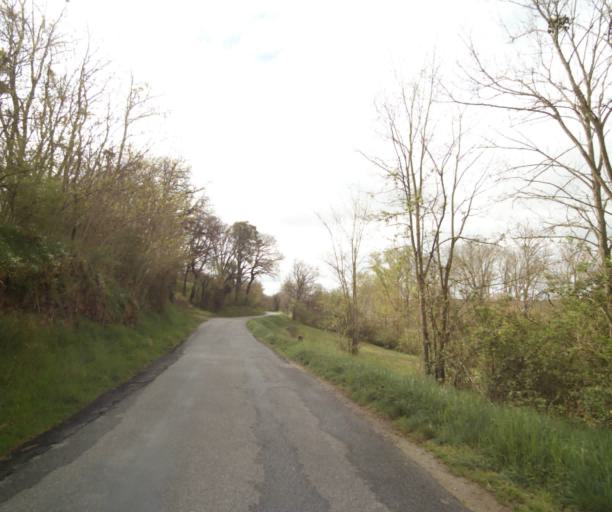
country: FR
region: Midi-Pyrenees
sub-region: Departement de l'Ariege
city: Saverdun
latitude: 43.2394
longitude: 1.5621
